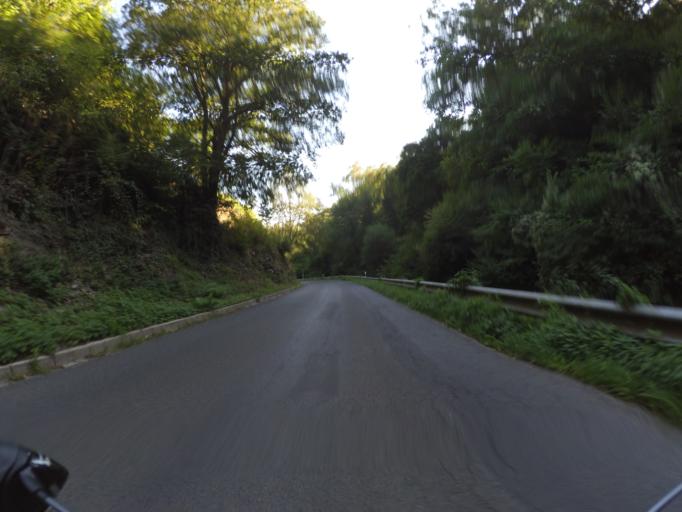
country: DE
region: Rheinland-Pfalz
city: Neumagen-Dhron
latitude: 49.8600
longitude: 6.8882
